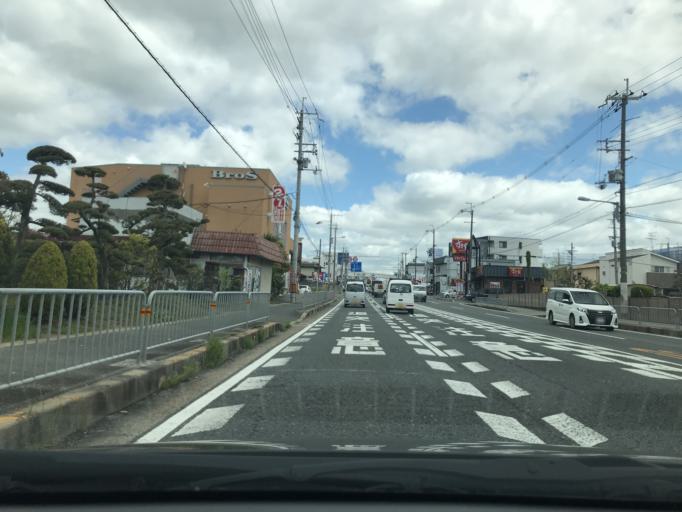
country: JP
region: Osaka
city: Mino
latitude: 34.8329
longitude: 135.4959
